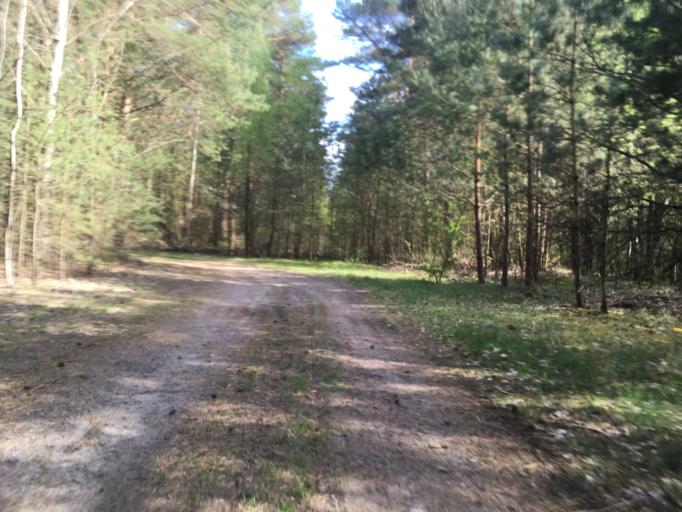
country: DE
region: Brandenburg
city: Bernau bei Berlin
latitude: 52.7065
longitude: 13.5748
